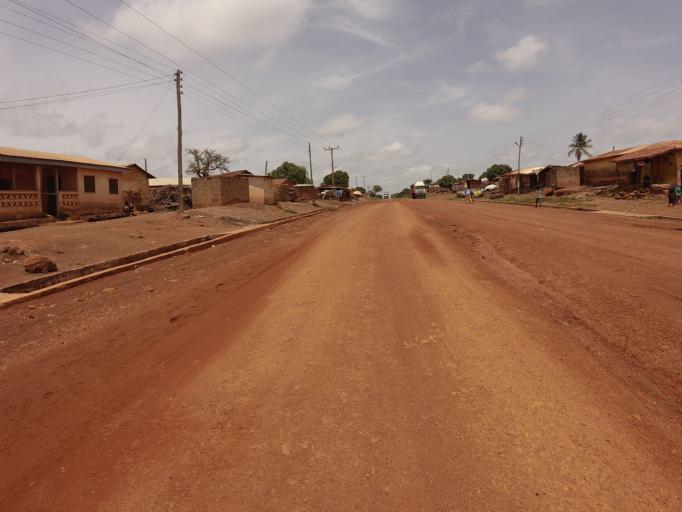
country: GH
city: Kpandae
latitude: 8.5948
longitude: 0.2366
